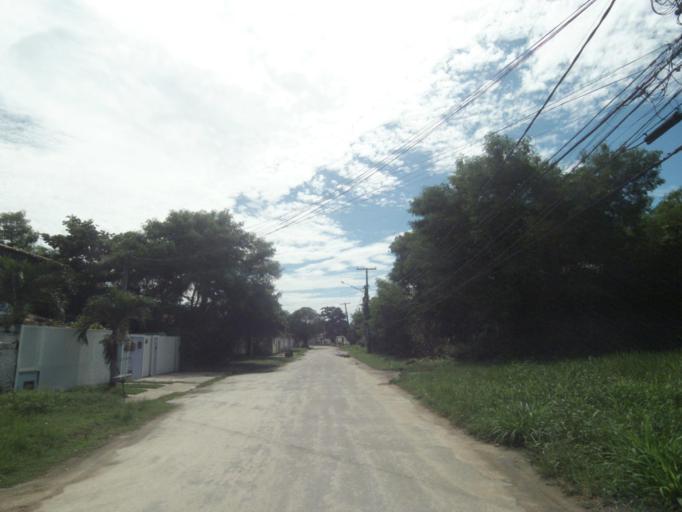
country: BR
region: Rio de Janeiro
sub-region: Niteroi
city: Niteroi
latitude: -22.9465
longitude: -43.0416
